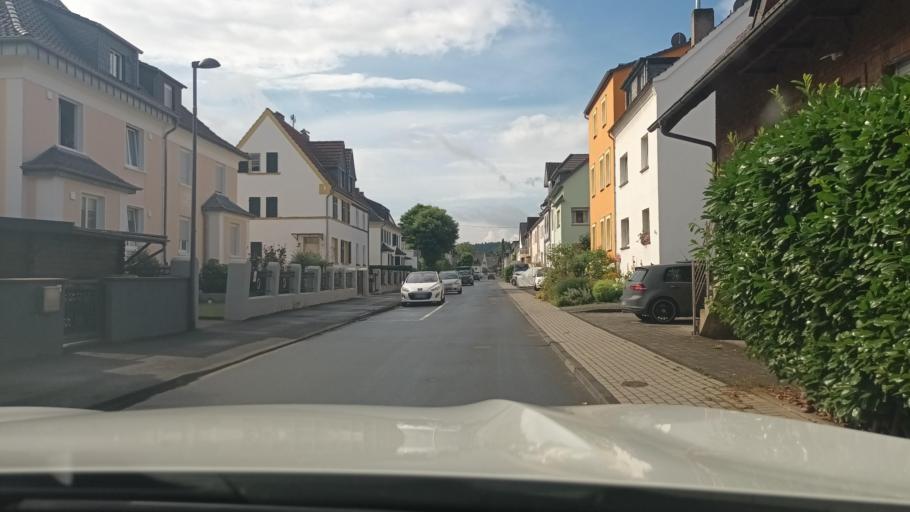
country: DE
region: North Rhine-Westphalia
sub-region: Regierungsbezirk Koln
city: Hennef
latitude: 50.7810
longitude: 7.2820
